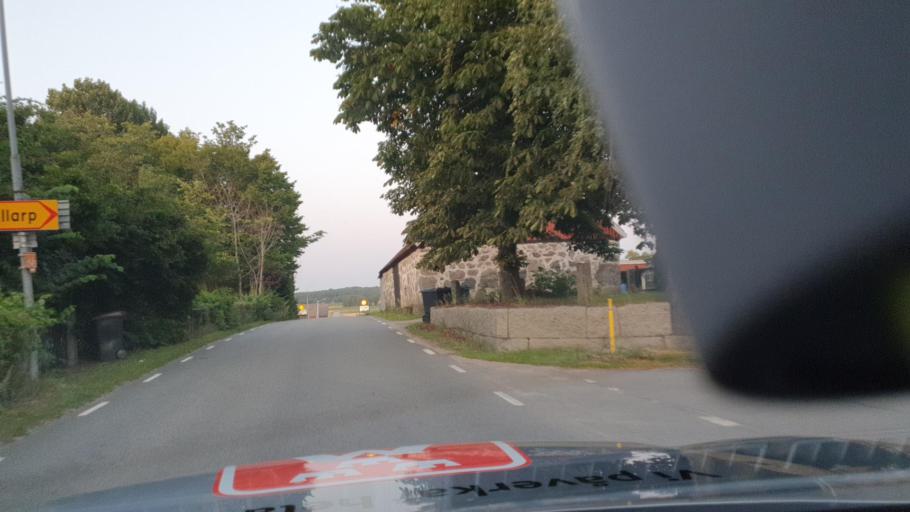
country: SE
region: Blekinge
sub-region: Solvesborgs Kommun
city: Soelvesborg
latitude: 56.0224
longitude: 14.6536
